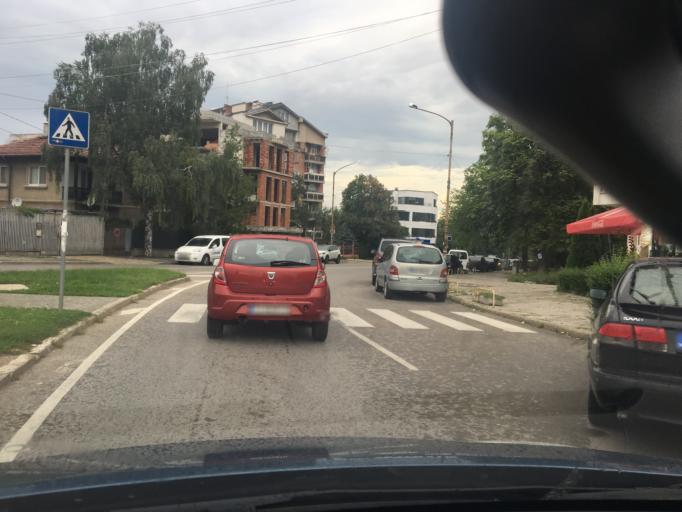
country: BG
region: Sofia-Capital
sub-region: Stolichna Obshtina
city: Sofia
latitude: 42.6645
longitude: 23.2660
